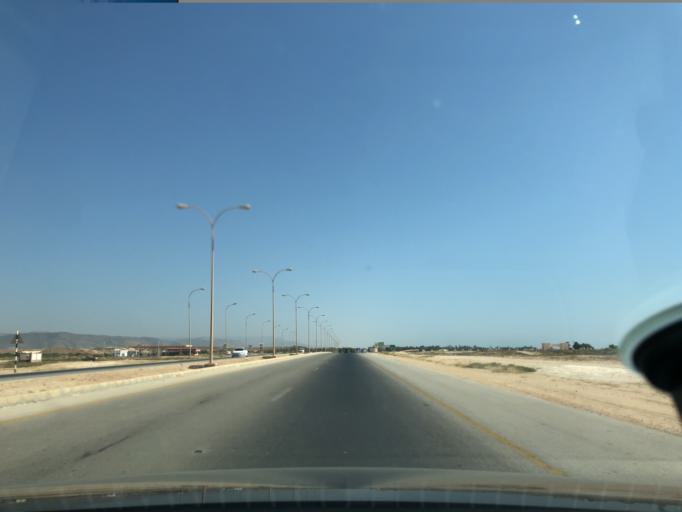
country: OM
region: Zufar
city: Salalah
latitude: 17.0398
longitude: 54.3648
